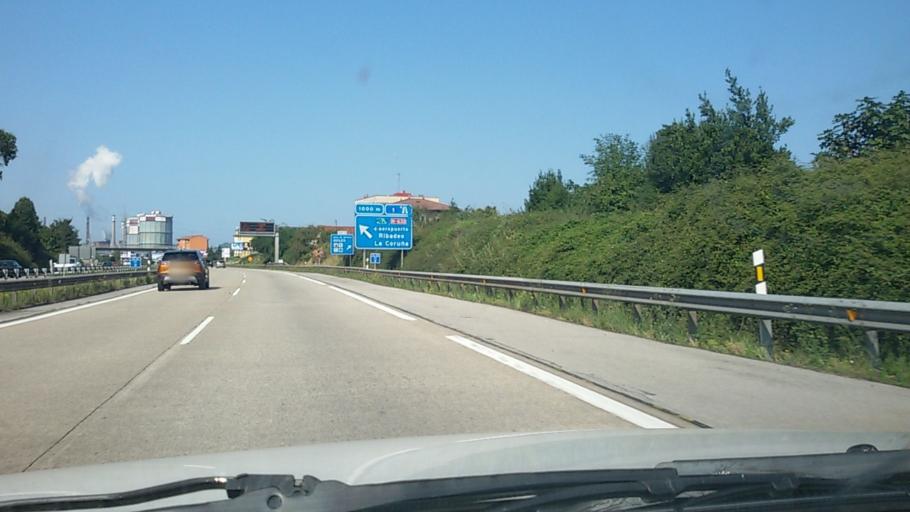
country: ES
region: Asturias
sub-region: Province of Asturias
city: Aviles
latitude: 43.5523
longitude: -5.8829
